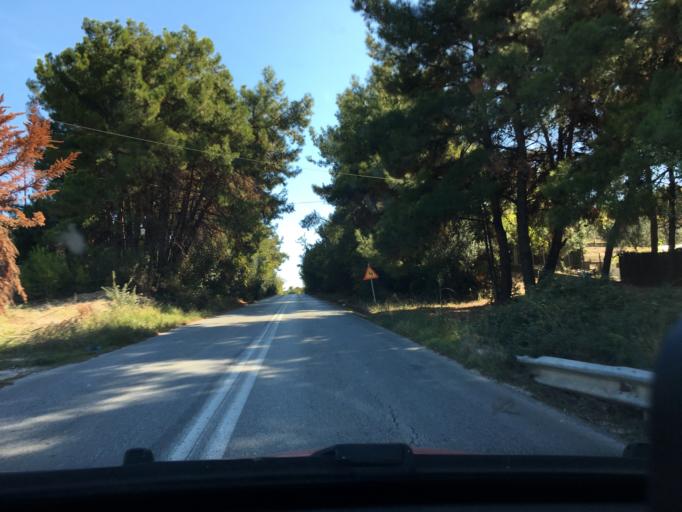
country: GR
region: Central Macedonia
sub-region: Nomos Chalkidikis
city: Ierissos
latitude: 40.3856
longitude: 23.8968
